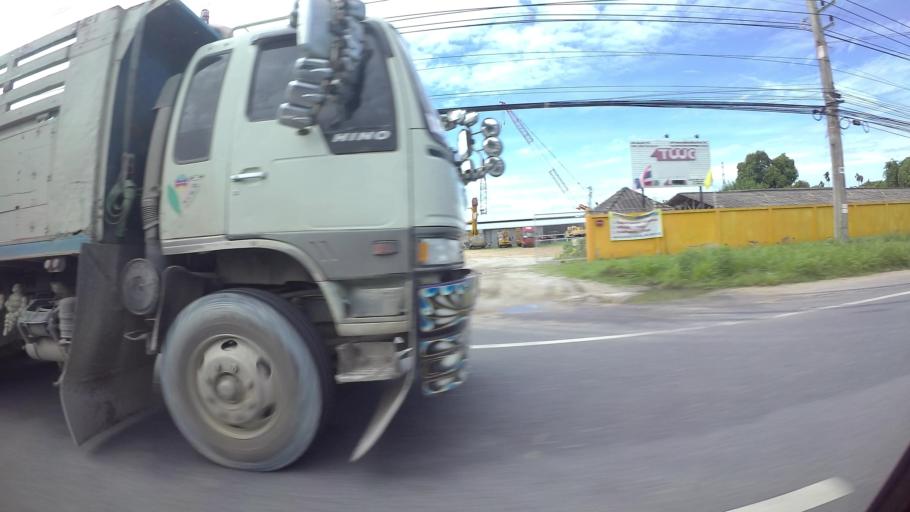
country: TH
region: Rayong
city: Ban Chang
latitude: 12.7441
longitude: 101.0944
